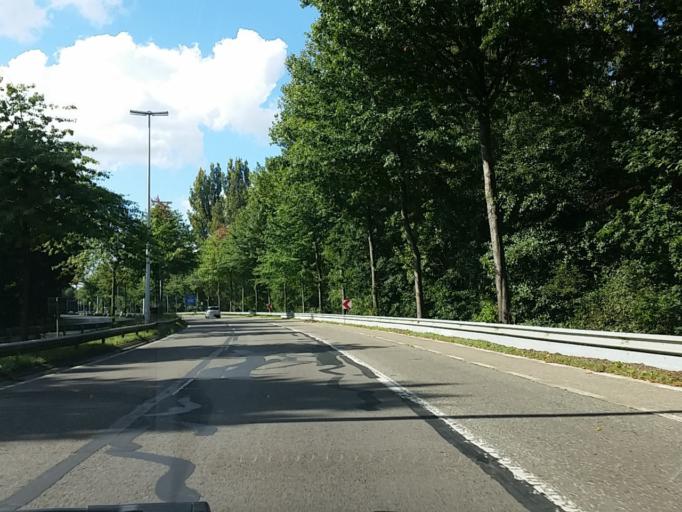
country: BE
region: Flanders
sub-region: Provincie Antwerpen
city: Wijnegem
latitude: 51.2341
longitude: 4.5405
